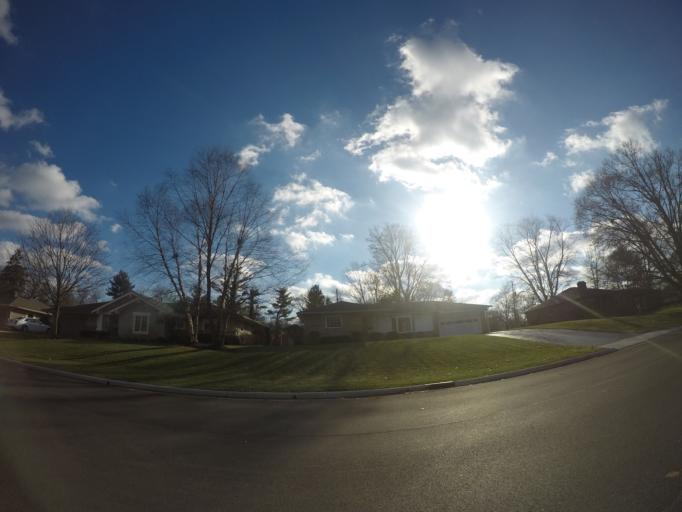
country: US
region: Ohio
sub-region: Franklin County
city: Upper Arlington
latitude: 40.0313
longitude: -83.0848
